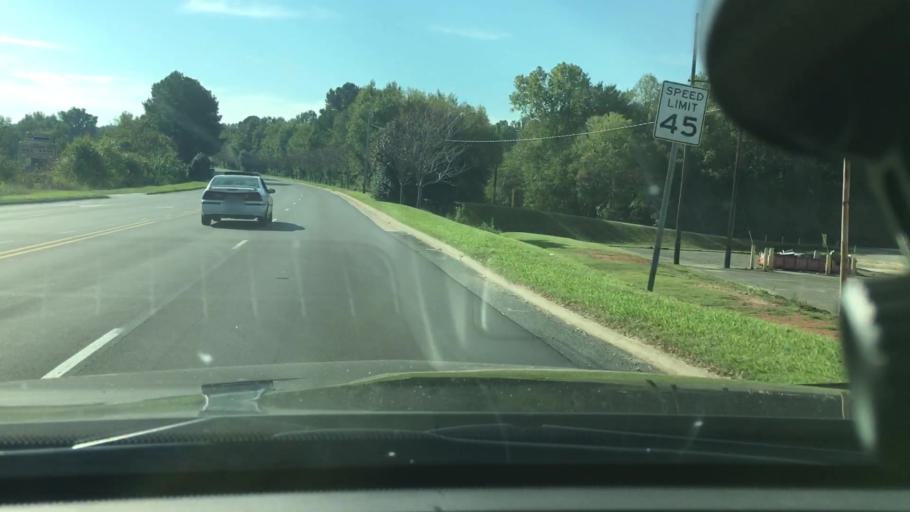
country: US
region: North Carolina
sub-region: Stanly County
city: Albemarle
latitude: 35.3456
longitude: -80.2040
